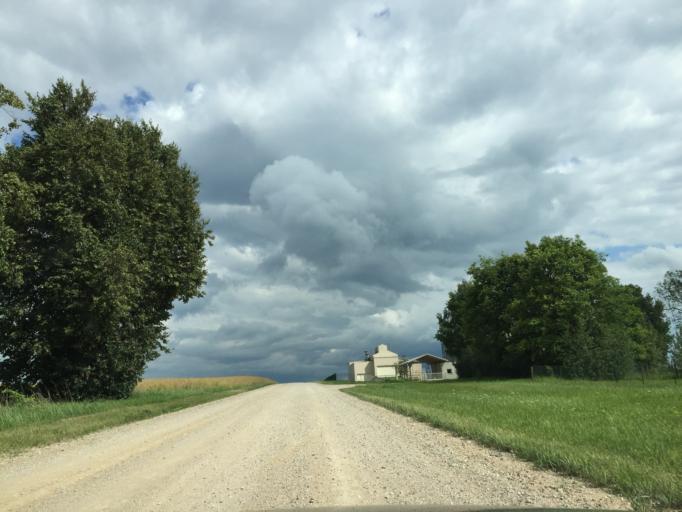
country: LV
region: Malpils
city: Malpils
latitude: 56.8587
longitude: 25.0263
